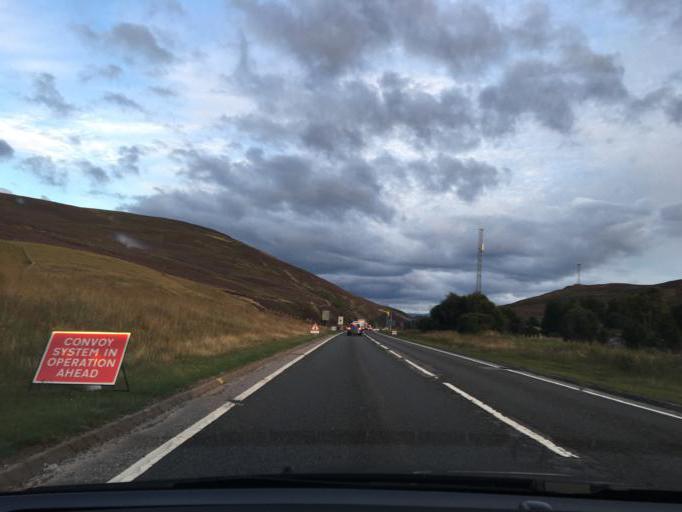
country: GB
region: Scotland
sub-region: Highland
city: Aviemore
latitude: 57.3083
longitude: -3.9391
